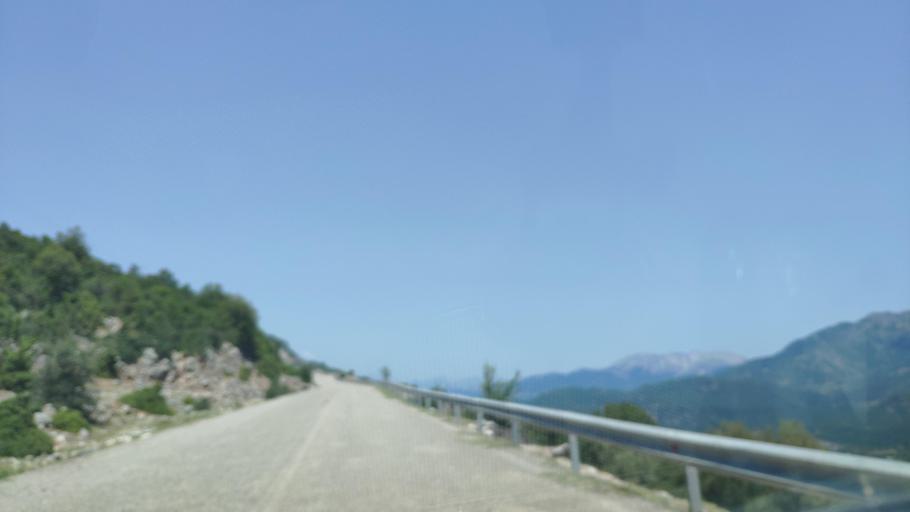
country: GR
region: Thessaly
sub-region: Nomos Kardhitsas
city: Anthiro
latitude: 39.1303
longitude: 21.3948
